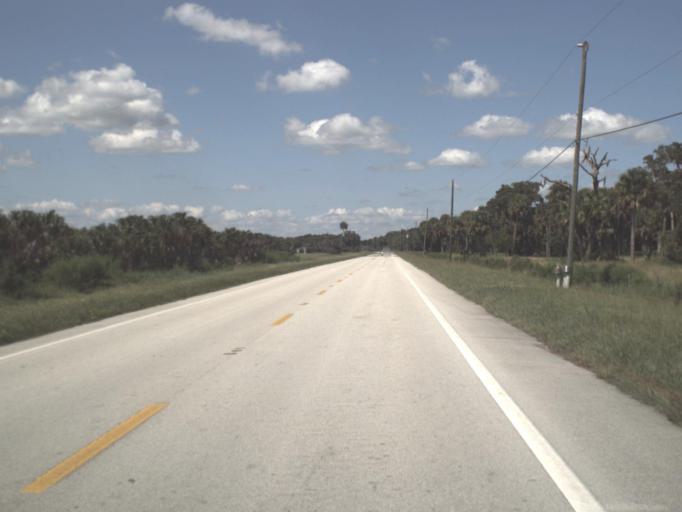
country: US
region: Florida
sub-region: Okeechobee County
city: Taylor Creek
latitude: 27.1748
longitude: -80.7277
